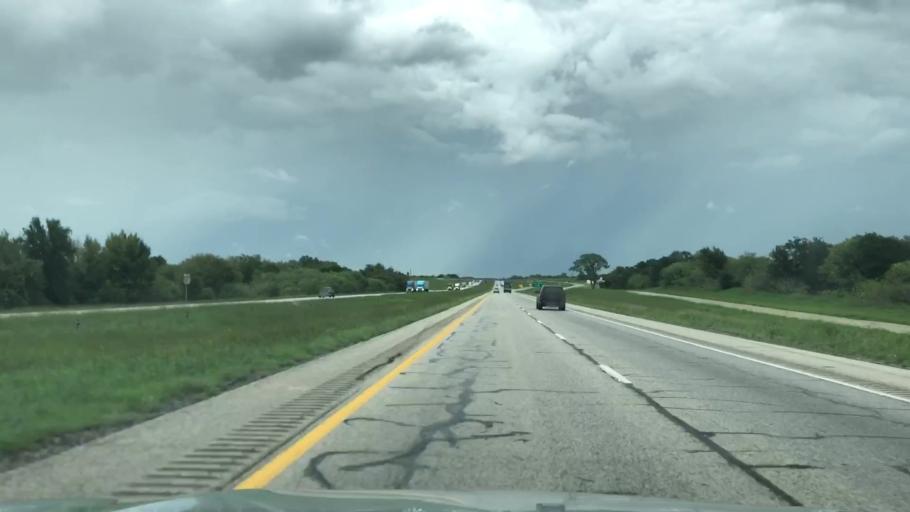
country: US
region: Texas
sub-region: Caldwell County
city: Luling
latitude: 29.6424
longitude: -97.7066
